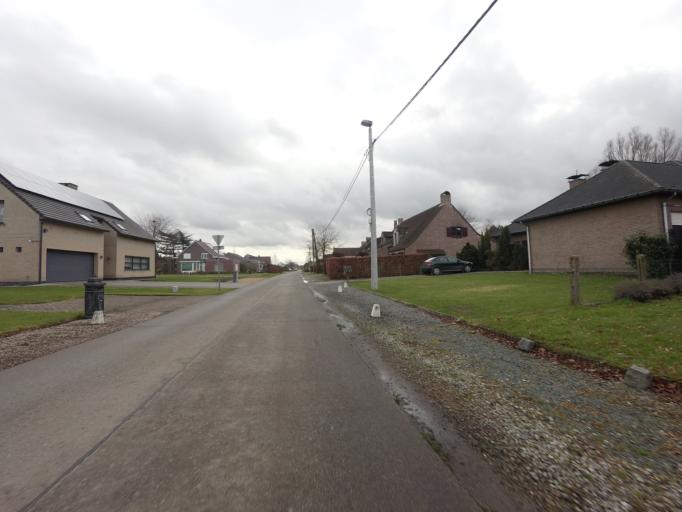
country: BE
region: Flanders
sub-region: Provincie Antwerpen
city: Duffel
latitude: 51.0821
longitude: 4.5023
